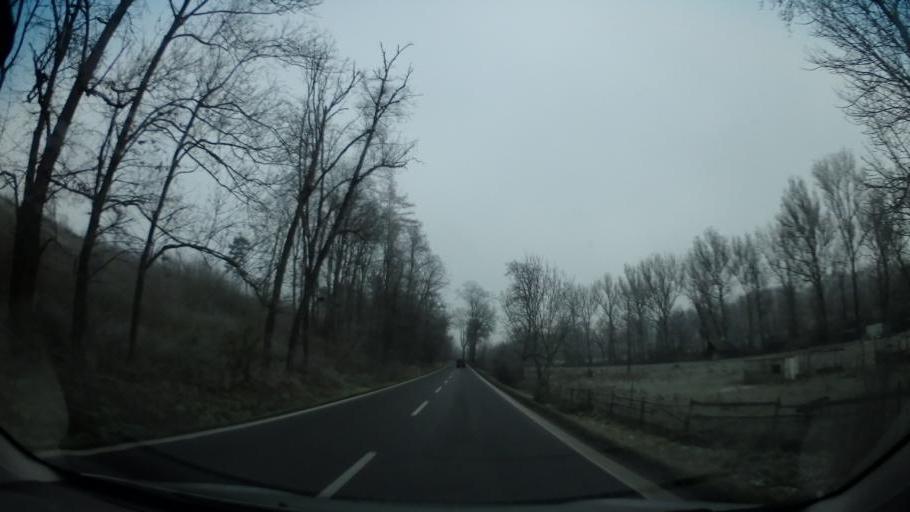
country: CZ
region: Vysocina
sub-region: Okres Trebic
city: Trebic
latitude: 49.2151
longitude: 15.9290
